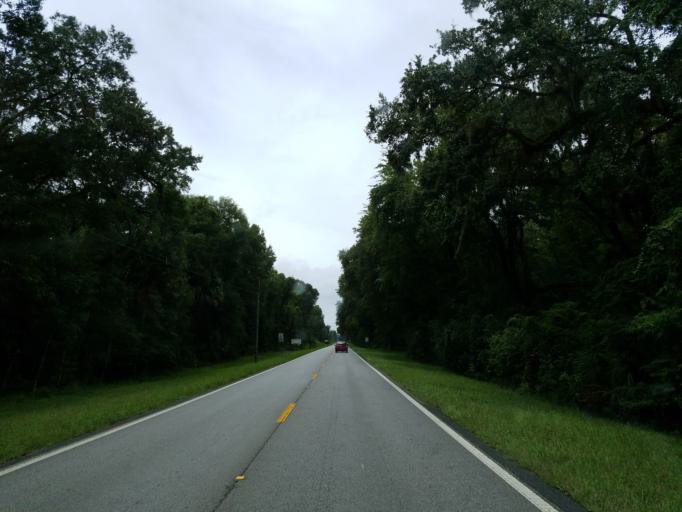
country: US
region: Florida
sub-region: Citrus County
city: Floral City
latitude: 28.7188
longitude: -82.2371
